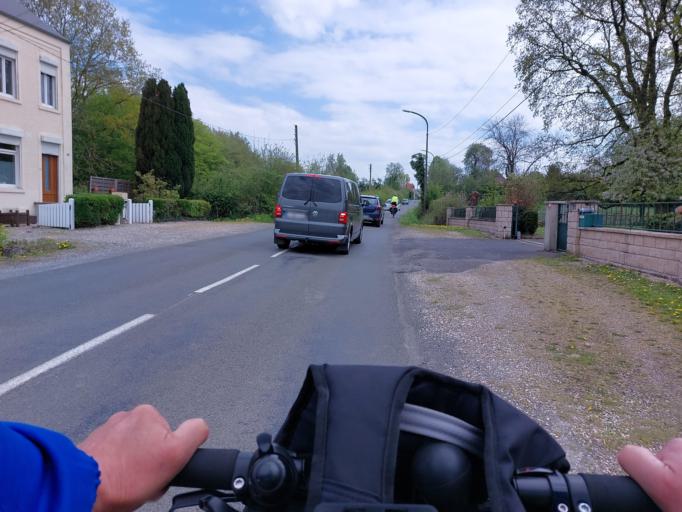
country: FR
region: Nord-Pas-de-Calais
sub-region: Departement du Nord
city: Hautmont
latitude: 50.2696
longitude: 3.8929
